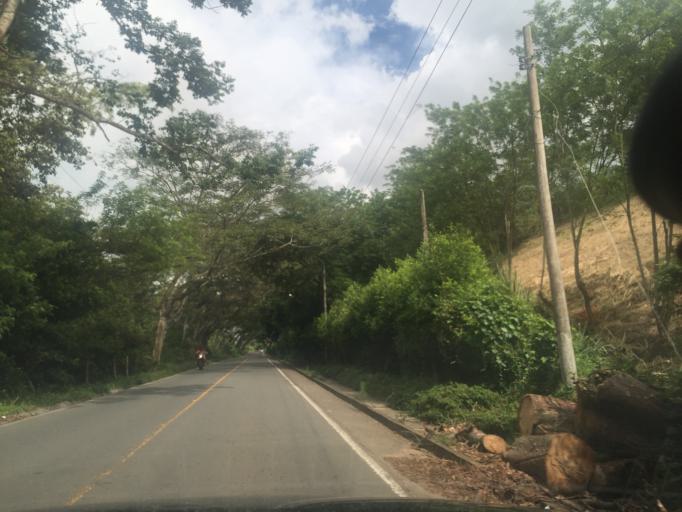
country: CO
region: Valle del Cauca
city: Caicedonia
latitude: 4.3414
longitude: -75.8397
